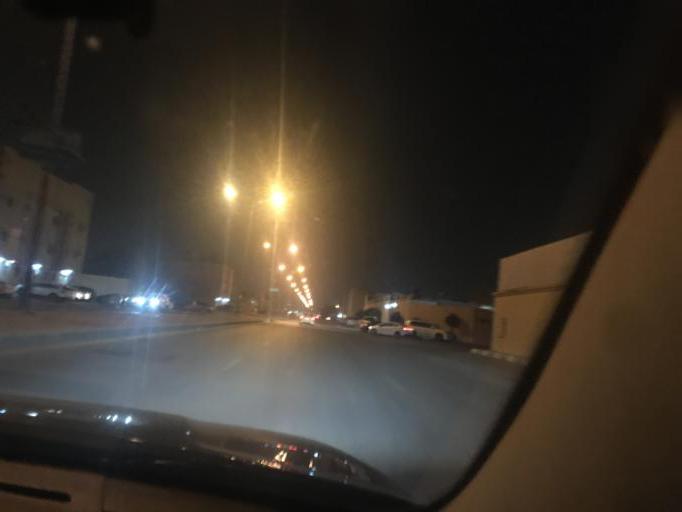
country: SA
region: Ar Riyad
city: Riyadh
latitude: 24.8237
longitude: 46.7404
